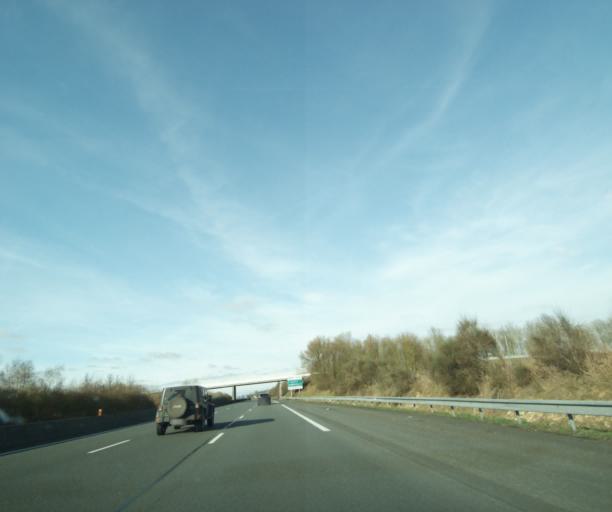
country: FR
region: Ile-de-France
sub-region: Departement de l'Essonne
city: Corbreuse
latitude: 48.4425
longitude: 1.9084
